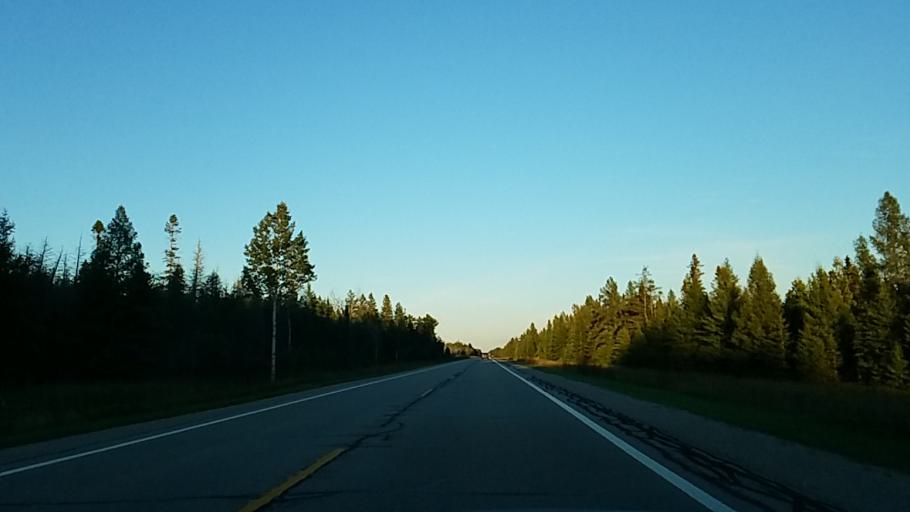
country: US
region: Michigan
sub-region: Alger County
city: Munising
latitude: 46.3468
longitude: -86.3814
